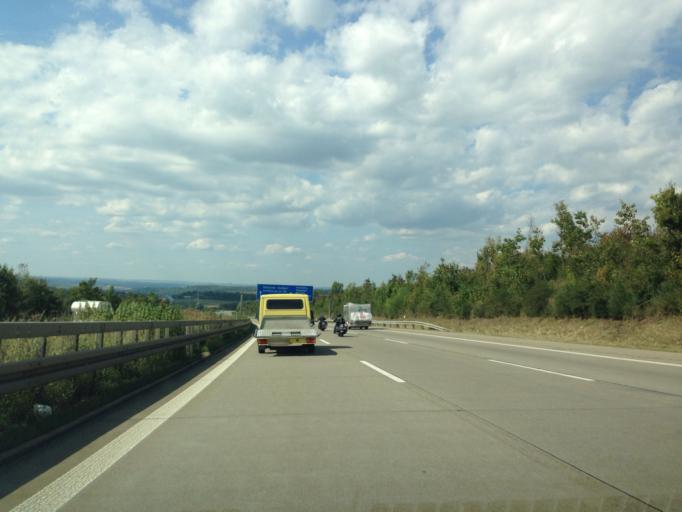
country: DE
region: Baden-Wuerttemberg
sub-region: Regierungsbezirk Stuttgart
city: Aichelberg
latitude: 48.6320
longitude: 9.5642
